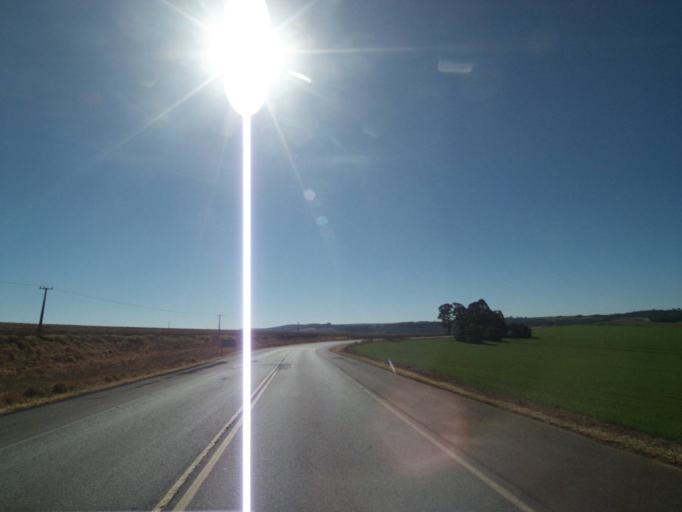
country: BR
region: Parana
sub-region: Tibagi
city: Tibagi
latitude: -24.3938
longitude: -50.3361
